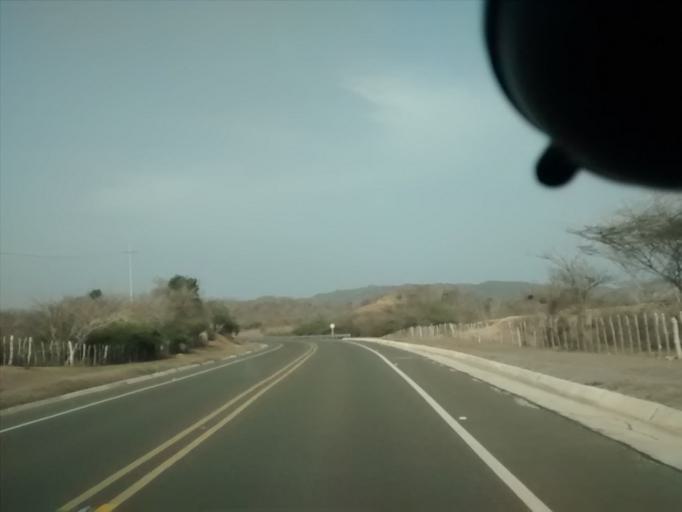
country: CO
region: Atlantico
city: Juan de Acosta
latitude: 10.8597
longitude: -75.1122
